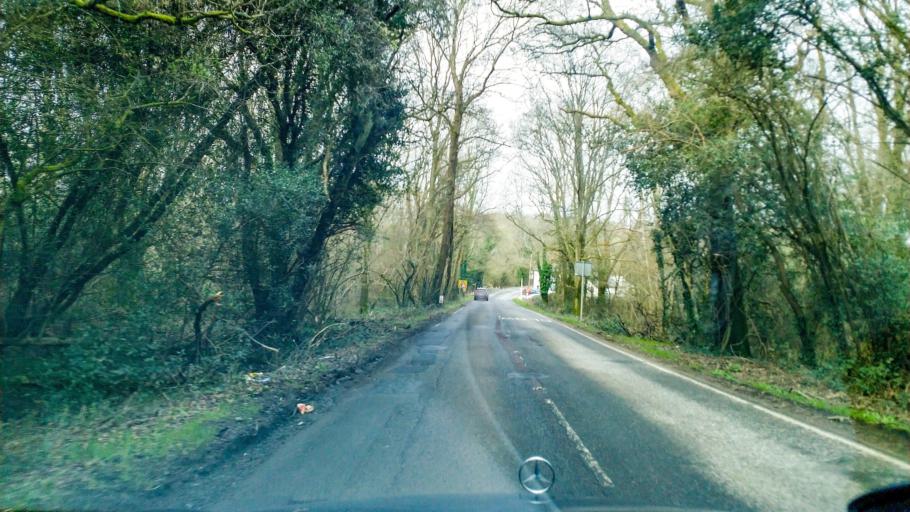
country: GB
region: England
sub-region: Surrey
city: Dorking
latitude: 51.2060
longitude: -0.3107
